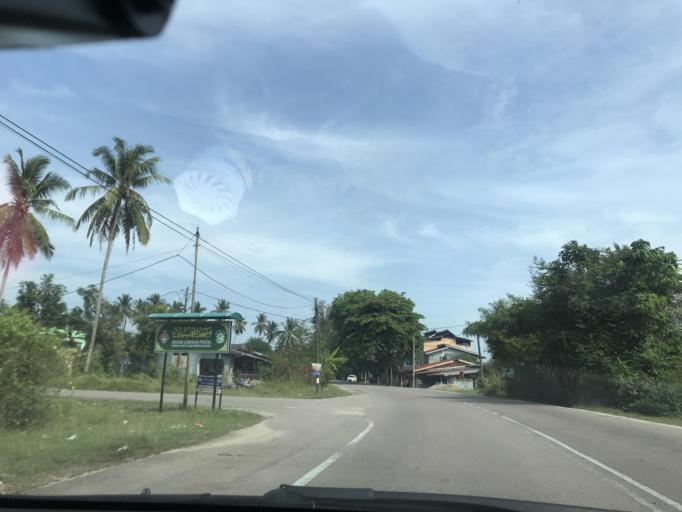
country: MY
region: Kelantan
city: Tumpat
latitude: 6.2082
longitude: 102.1412
